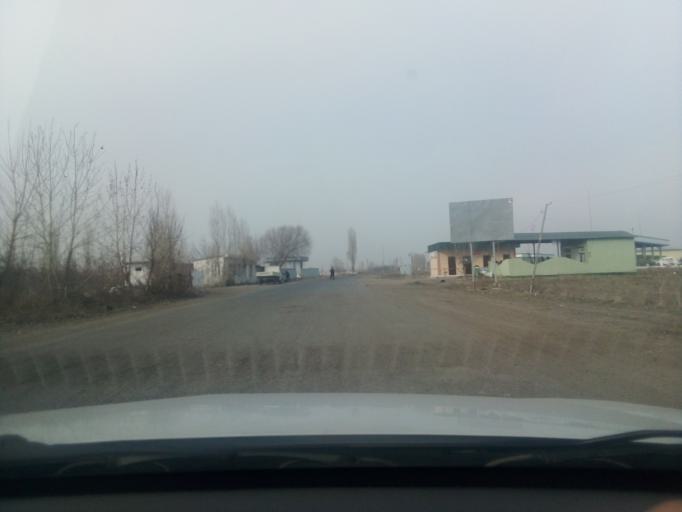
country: UZ
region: Namangan
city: Pop Shahri
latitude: 40.9082
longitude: 71.1021
